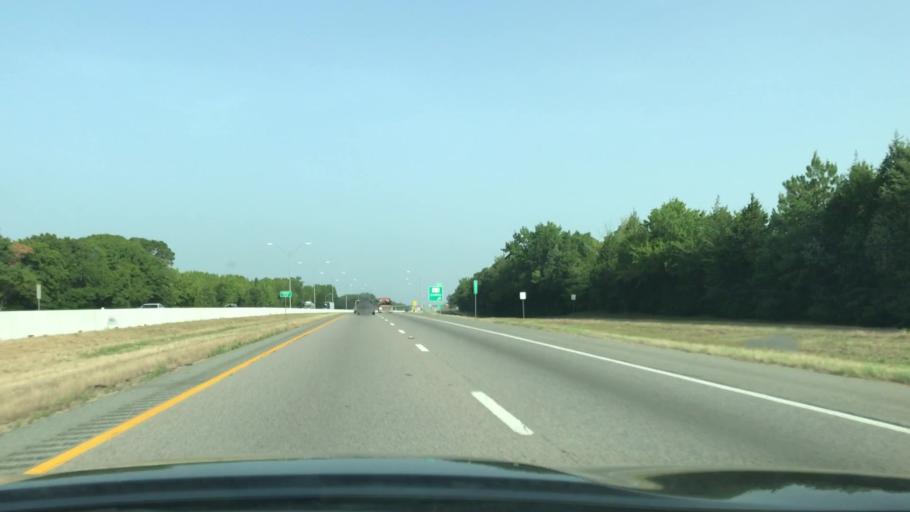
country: US
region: Texas
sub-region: Van Zandt County
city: Canton
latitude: 32.5566
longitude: -95.7988
